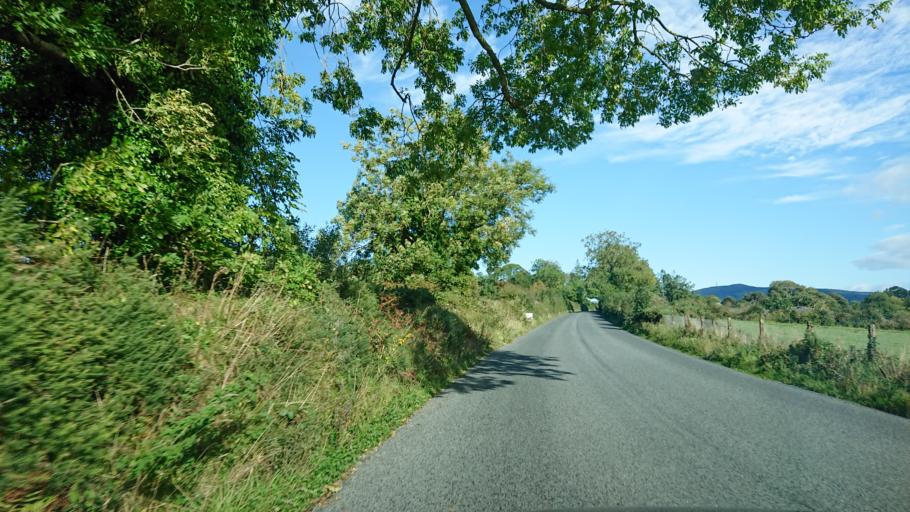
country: IE
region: Munster
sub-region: Waterford
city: Dungarvan
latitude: 52.1567
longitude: -7.6958
